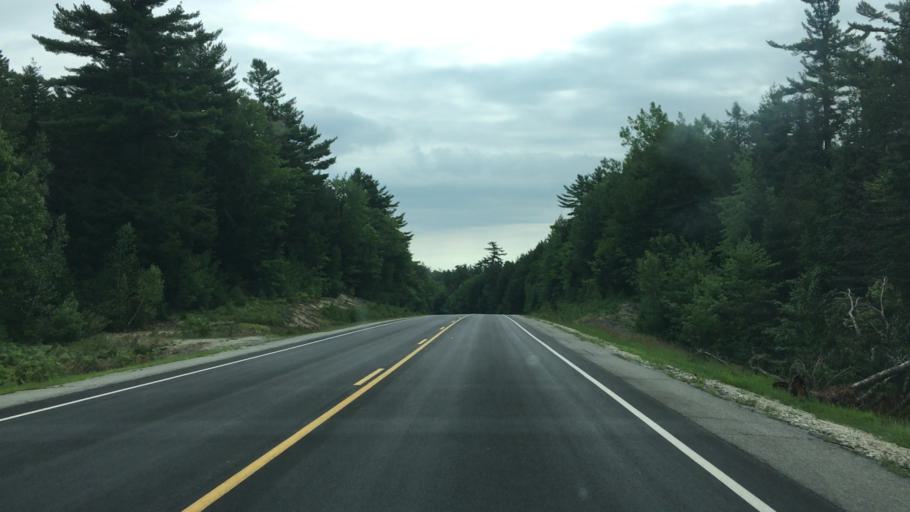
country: US
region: Maine
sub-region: Washington County
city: Addison
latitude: 44.9091
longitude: -67.8458
